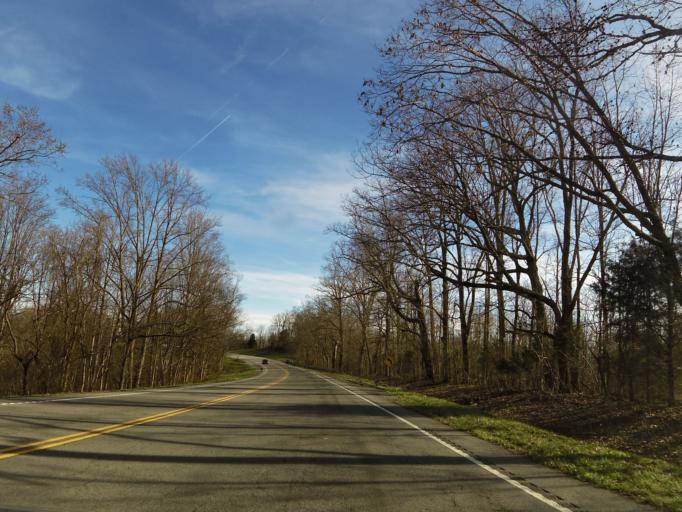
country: US
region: Tennessee
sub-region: Cannon County
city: Woodbury
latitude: 35.8099
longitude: -86.0277
